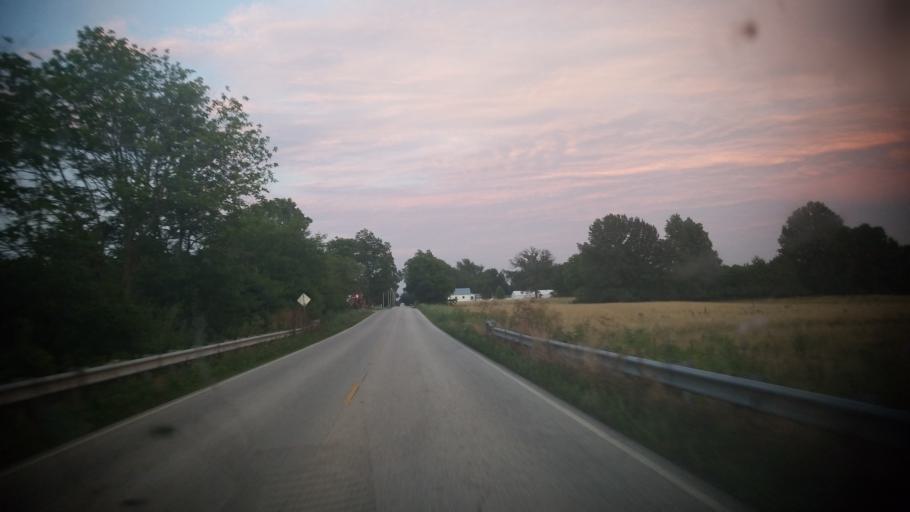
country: US
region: Illinois
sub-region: Clay County
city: Flora
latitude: 38.5159
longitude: -88.4460
